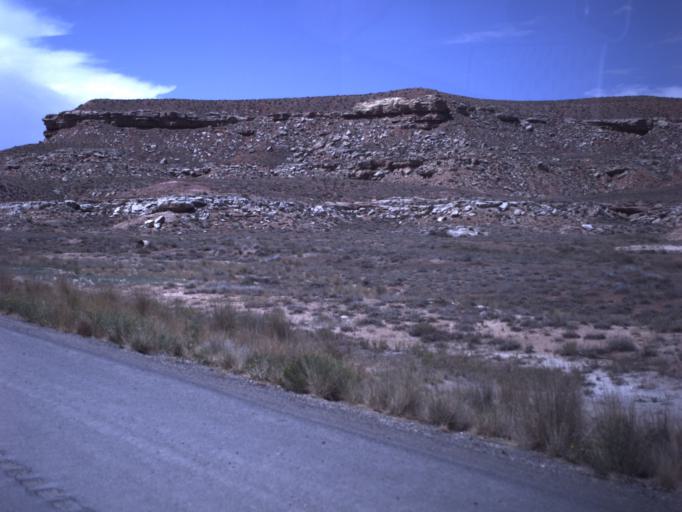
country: US
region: Utah
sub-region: Uintah County
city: Maeser
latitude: 40.3154
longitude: -109.6994
